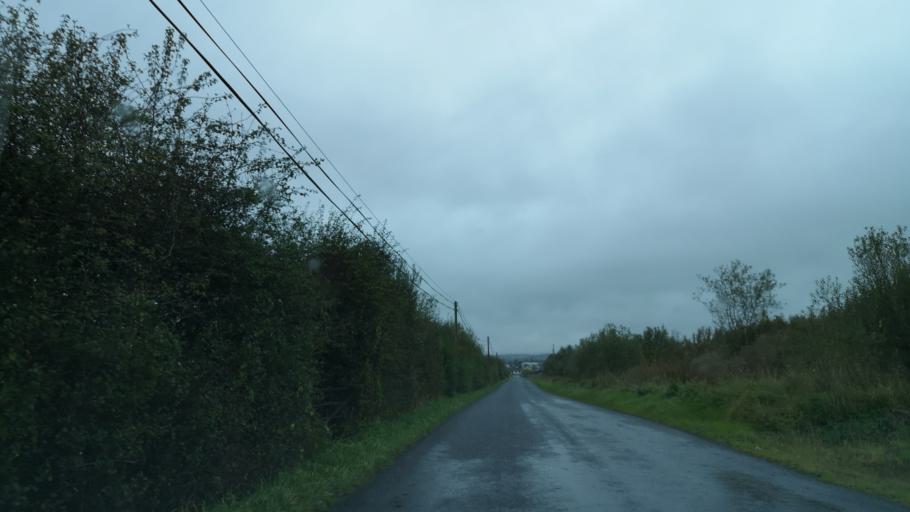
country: IE
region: Connaught
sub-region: Roscommon
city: Ballaghaderreen
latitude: 53.8945
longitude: -8.5750
